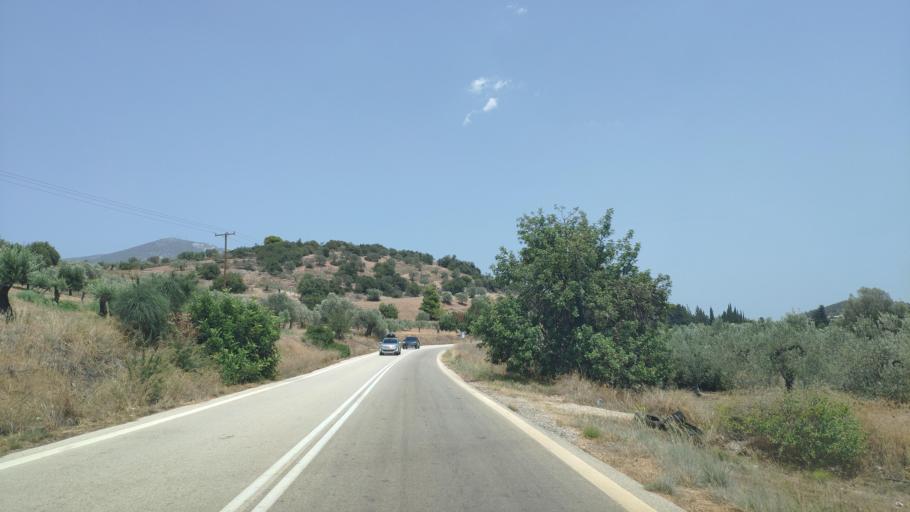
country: GR
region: Peloponnese
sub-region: Nomos Argolidos
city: Didyma
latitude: 37.4306
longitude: 23.1617
